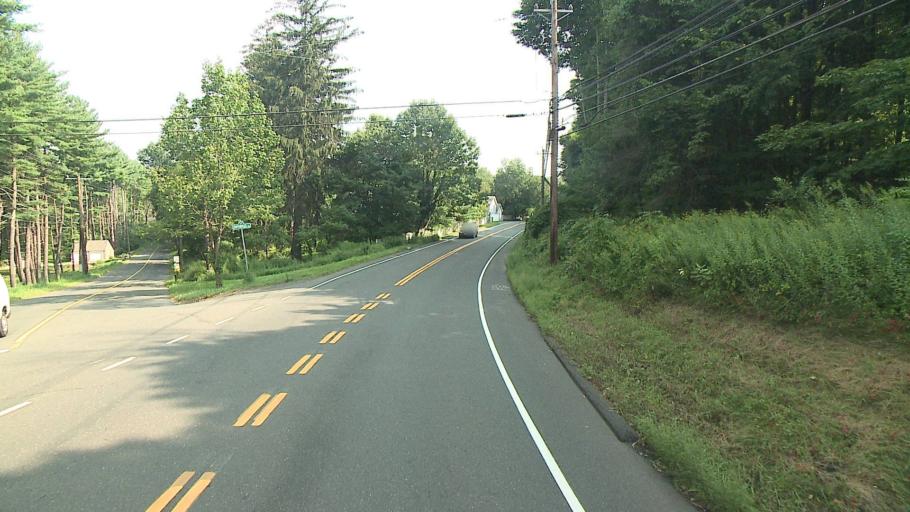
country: US
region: Connecticut
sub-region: Fairfield County
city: Georgetown
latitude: 41.2747
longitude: -73.4203
